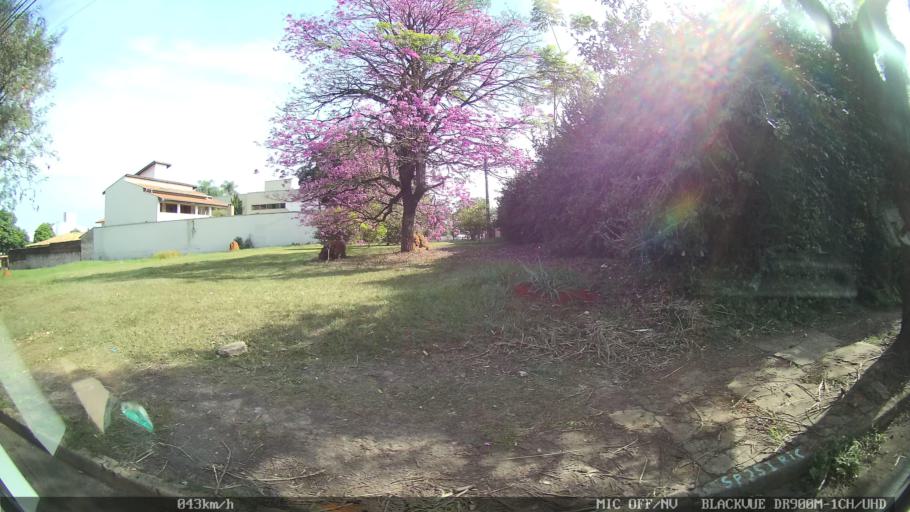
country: BR
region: Sao Paulo
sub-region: Piracicaba
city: Piracicaba
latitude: -22.7213
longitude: -47.6641
